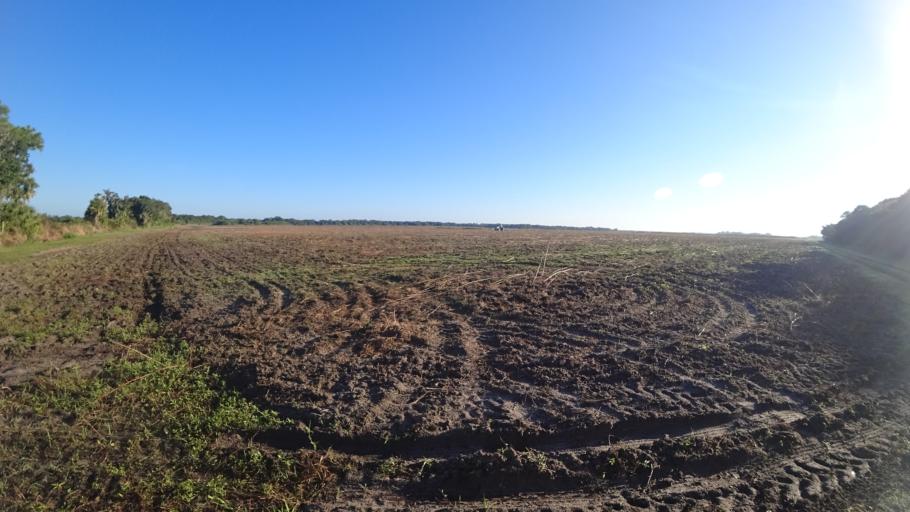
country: US
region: Florida
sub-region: Manatee County
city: Memphis
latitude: 27.6309
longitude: -82.5147
